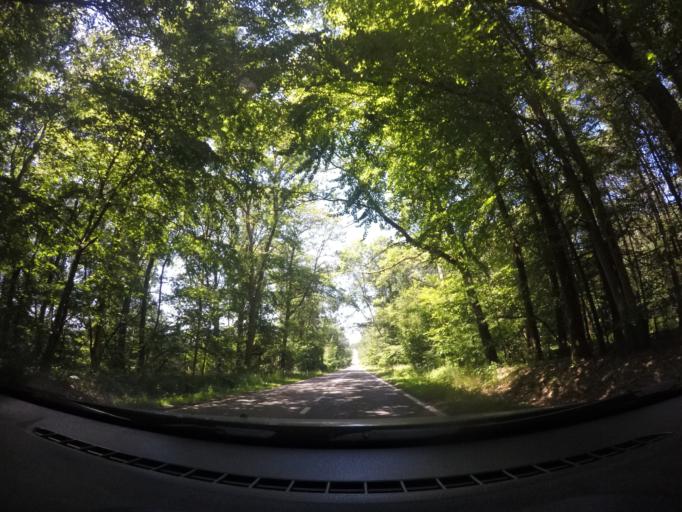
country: BE
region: Wallonia
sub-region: Province du Luxembourg
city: Daverdisse
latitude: 50.0170
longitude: 5.1712
